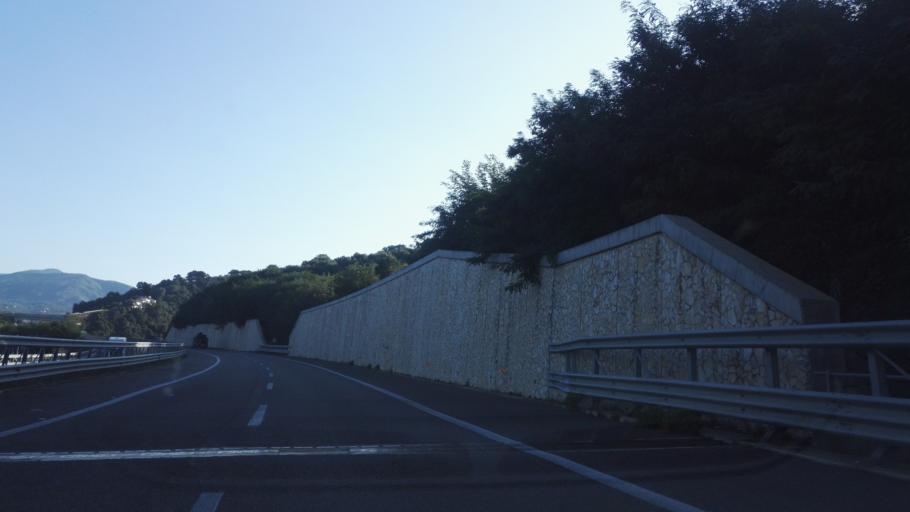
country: IT
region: Calabria
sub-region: Provincia di Catanzaro
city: Nocera Scalo
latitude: 39.0317
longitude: 16.1328
